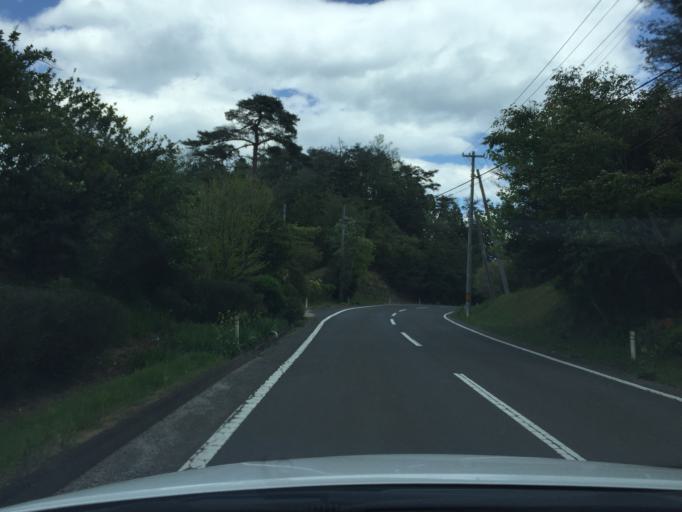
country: JP
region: Miyagi
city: Marumori
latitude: 37.7579
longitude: 140.9558
